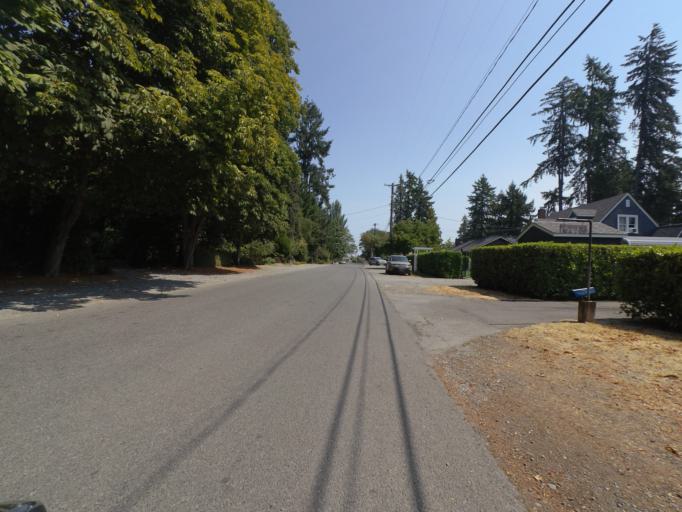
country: US
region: Washington
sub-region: Pierce County
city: Lakewood
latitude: 47.1606
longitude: -122.5236
